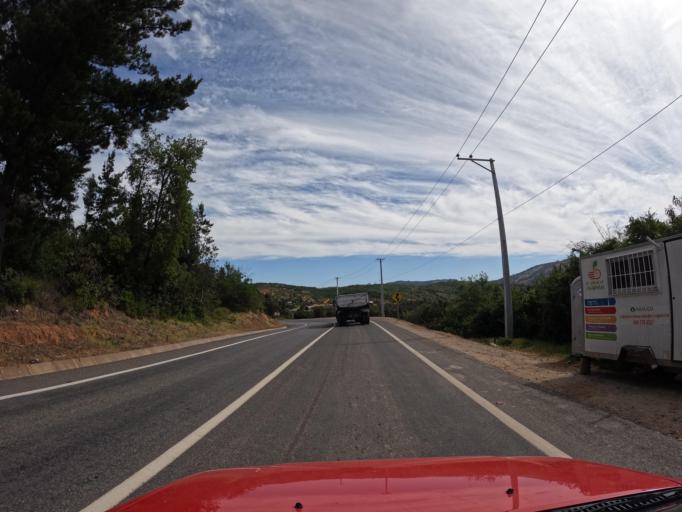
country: CL
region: Maule
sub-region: Provincia de Talca
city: Talca
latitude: -35.1669
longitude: -71.9734
